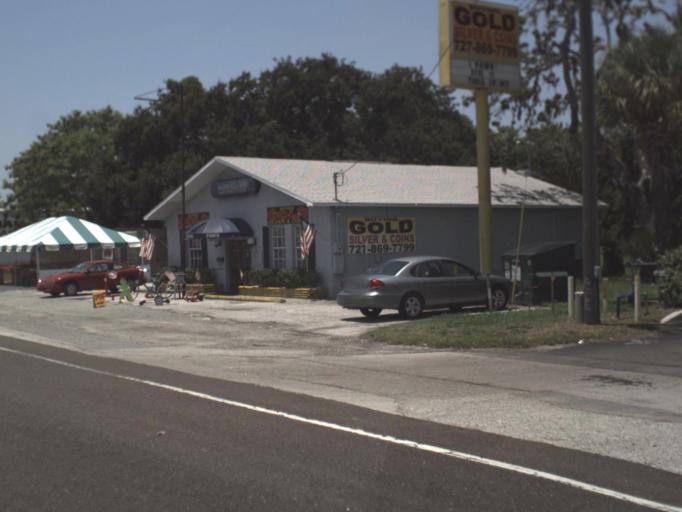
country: US
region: Florida
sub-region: Pasco County
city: Hudson
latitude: 28.3631
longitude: -82.6943
